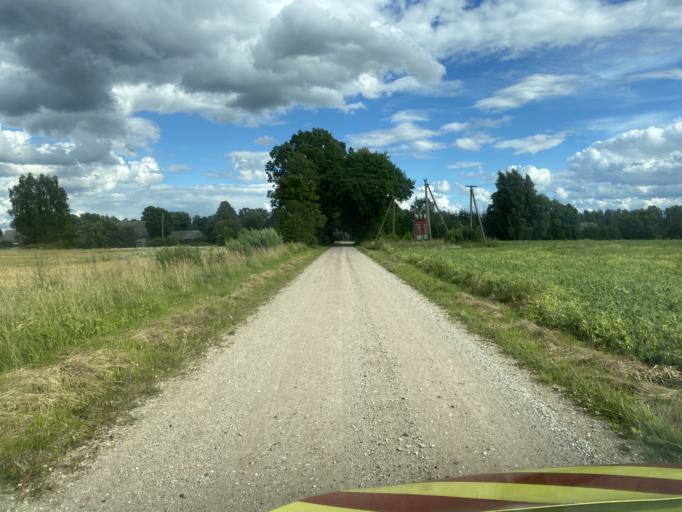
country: EE
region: Viljandimaa
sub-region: Viiratsi vald
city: Viiratsi
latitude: 58.3974
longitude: 25.8173
